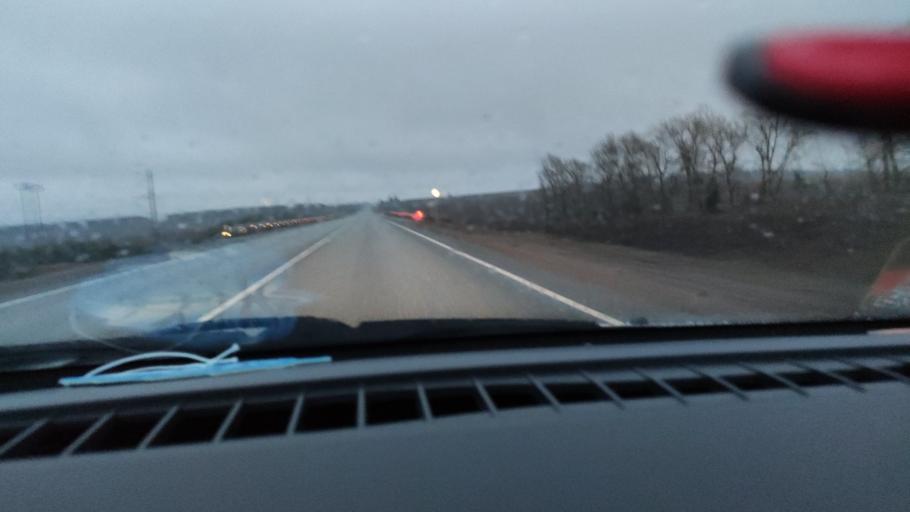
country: RU
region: Udmurtiya
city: Alnashi
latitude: 56.2403
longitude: 52.3955
